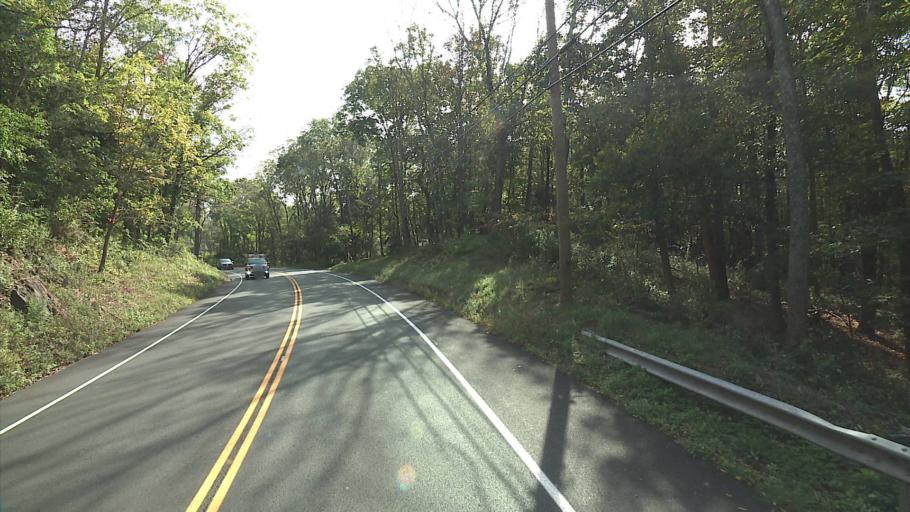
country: US
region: Connecticut
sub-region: Fairfield County
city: Newtown
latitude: 41.4013
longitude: -73.2479
